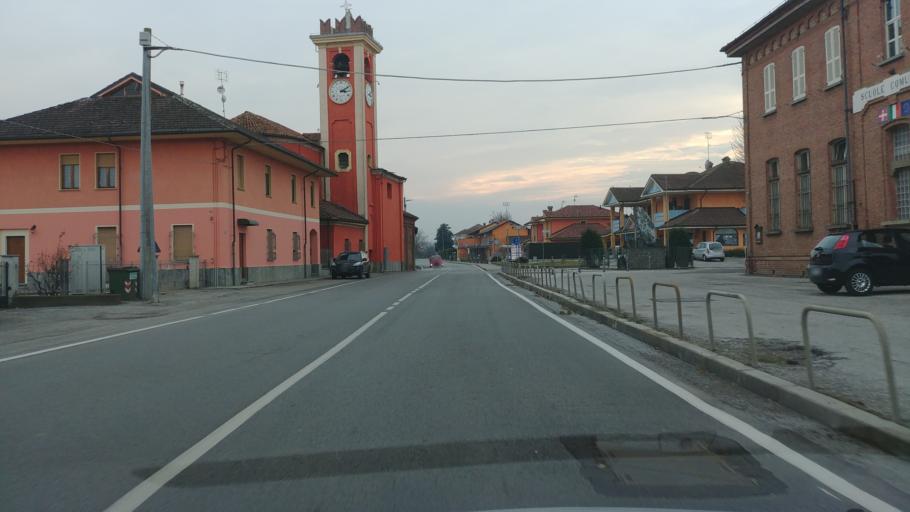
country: IT
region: Piedmont
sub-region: Provincia di Cuneo
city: Sant'Albano Stura
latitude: 44.5117
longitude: 7.6894
